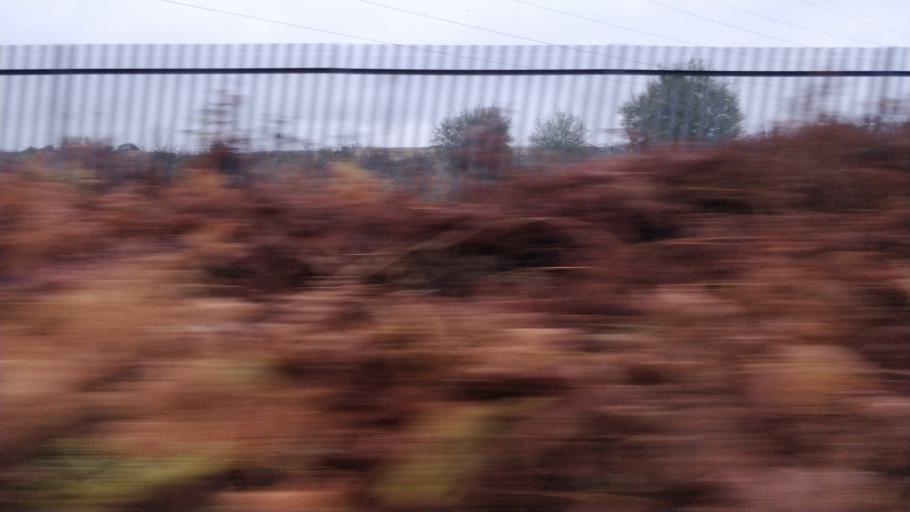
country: GB
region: England
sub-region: Borough of Wigan
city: Tyldesley
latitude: 53.5279
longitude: -2.4639
